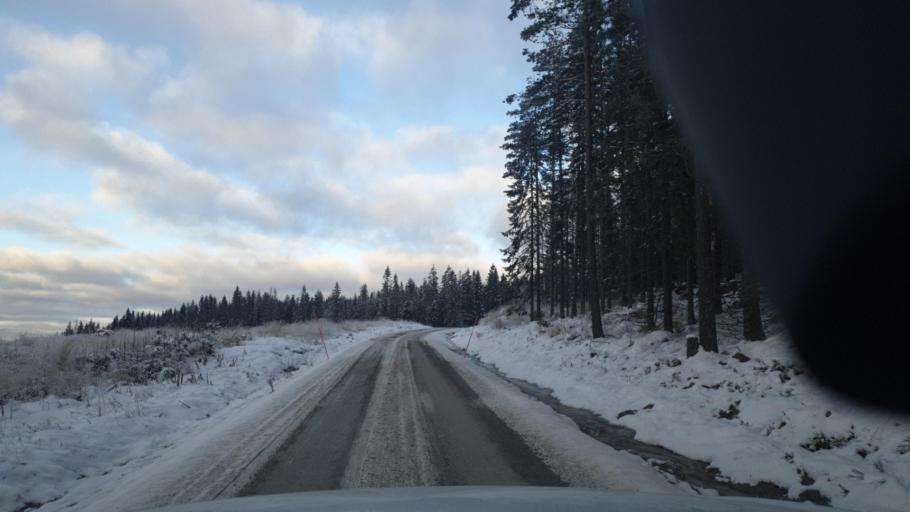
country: SE
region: Vaermland
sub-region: Eda Kommun
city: Charlottenberg
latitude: 60.0463
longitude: 12.6299
